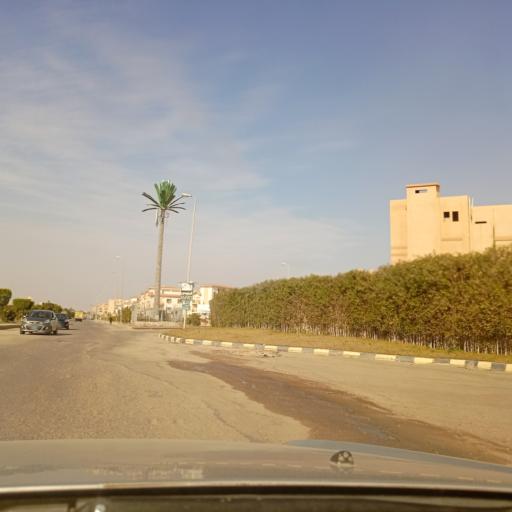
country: EG
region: Muhafazat al Qalyubiyah
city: Al Khankah
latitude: 30.0373
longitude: 31.4852
